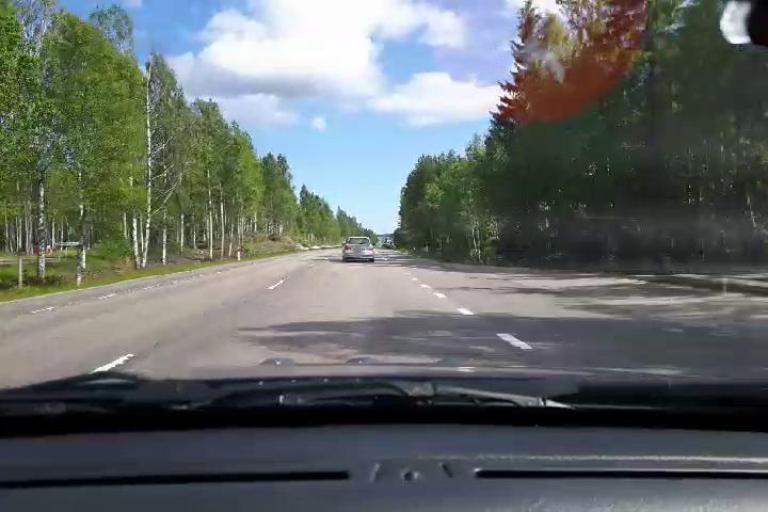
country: SE
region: Gaevleborg
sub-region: Hudiksvalls Kommun
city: Sorforsa
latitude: 61.7194
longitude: 17.0240
